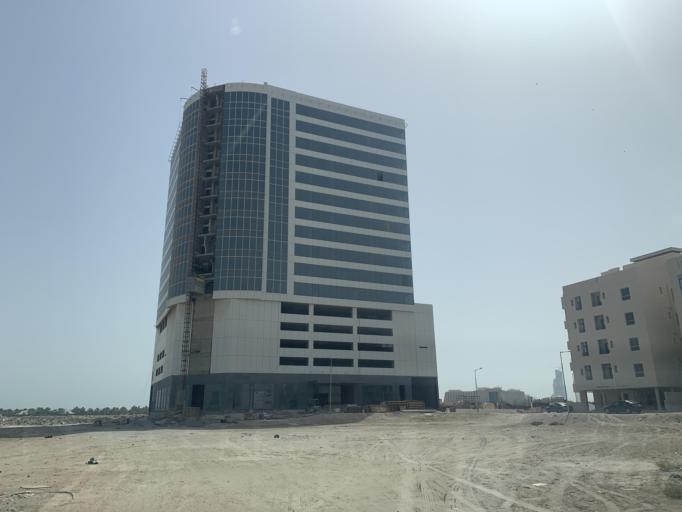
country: BH
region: Manama
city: Jidd Hafs
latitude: 26.2422
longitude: 50.5301
